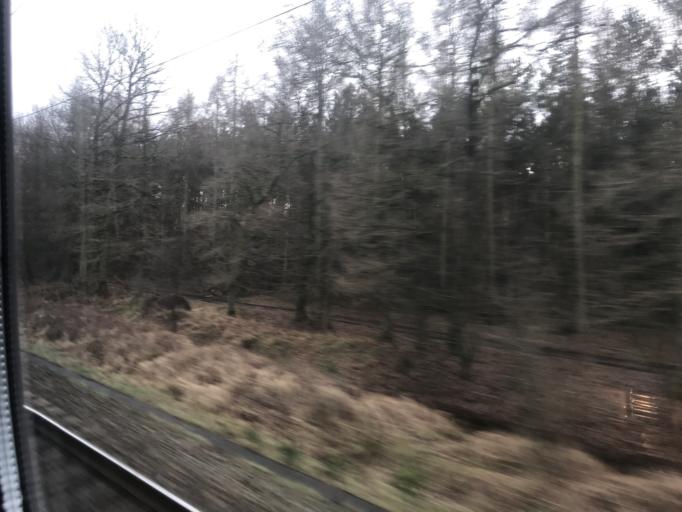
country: DE
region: Lower Saxony
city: Isenbuttel
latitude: 52.4507
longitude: 10.5649
